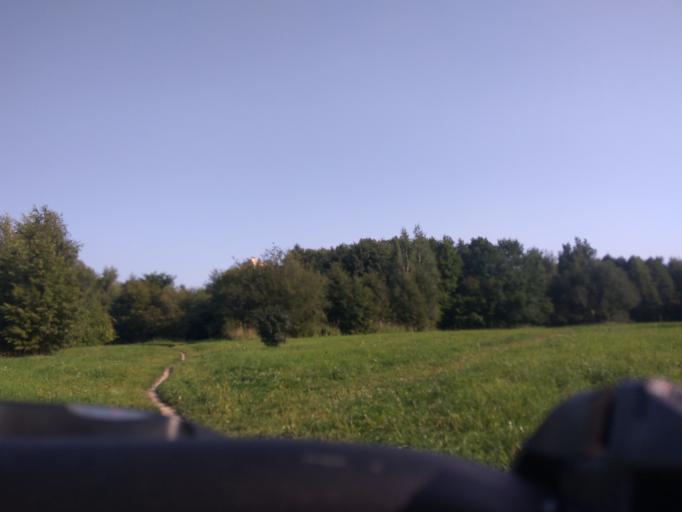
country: RU
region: Moscow
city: Orekhovo-Borisovo Severnoye
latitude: 55.6227
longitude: 37.6900
